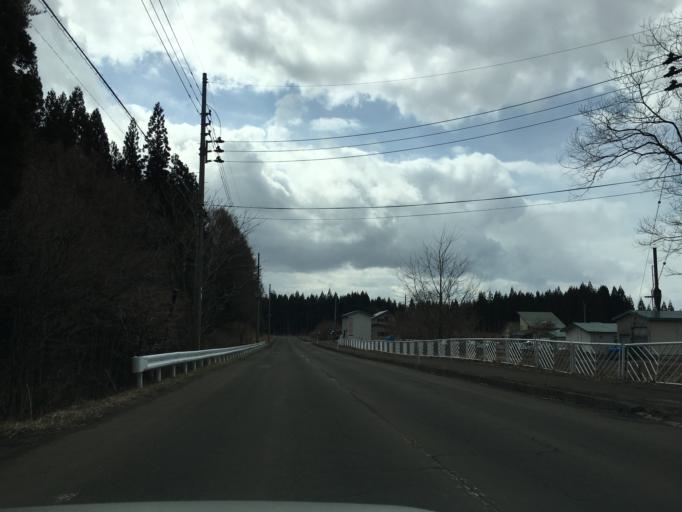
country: JP
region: Akita
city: Takanosu
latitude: 40.1838
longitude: 140.3528
